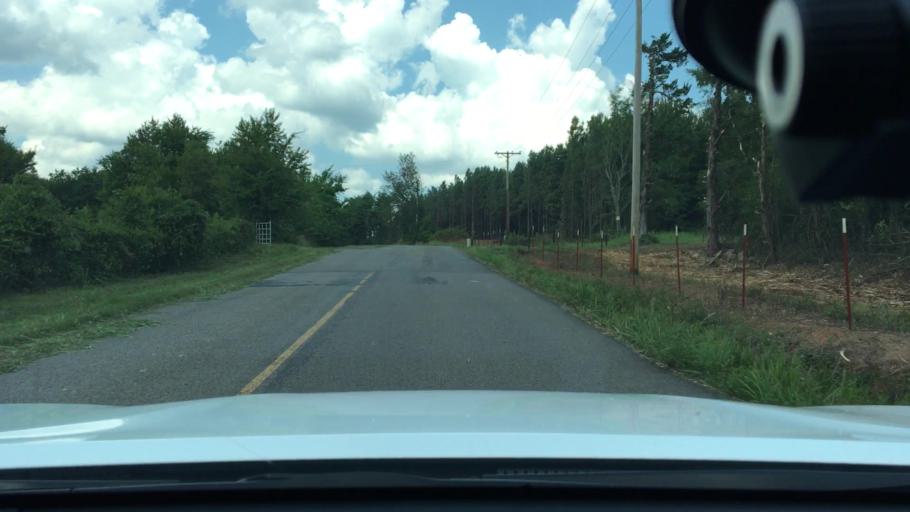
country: US
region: Arkansas
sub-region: Logan County
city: Paris
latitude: 35.2694
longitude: -93.6731
